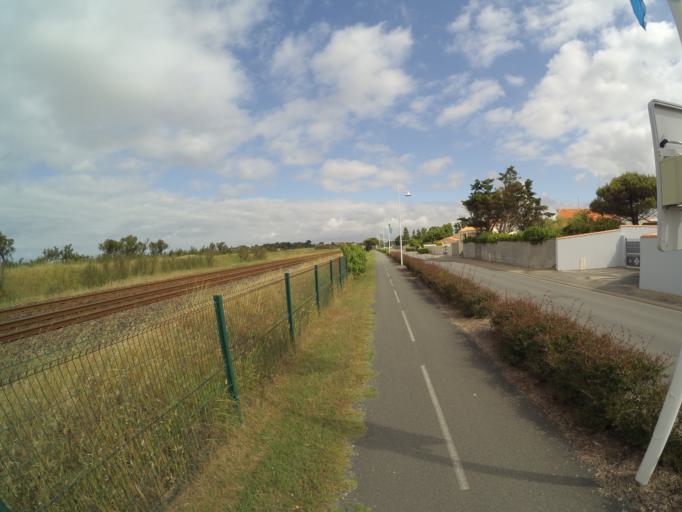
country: FR
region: Poitou-Charentes
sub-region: Departement de la Charente-Maritime
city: Angoulins
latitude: 46.0907
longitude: -1.0990
